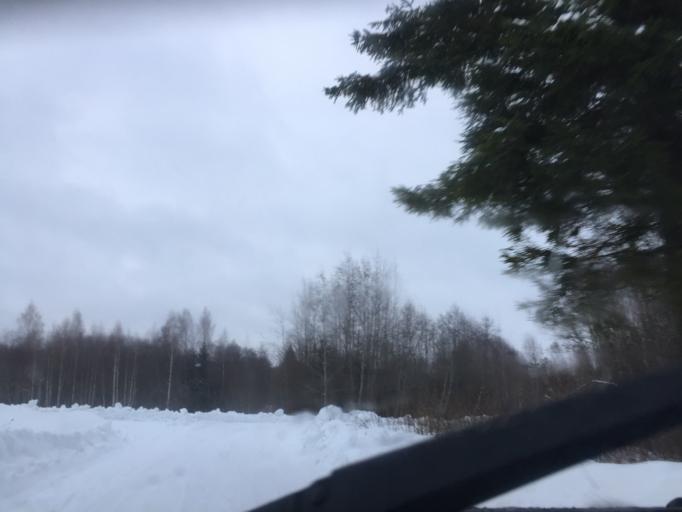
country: LV
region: Amatas Novads
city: Drabesi
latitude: 57.2053
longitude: 25.2987
